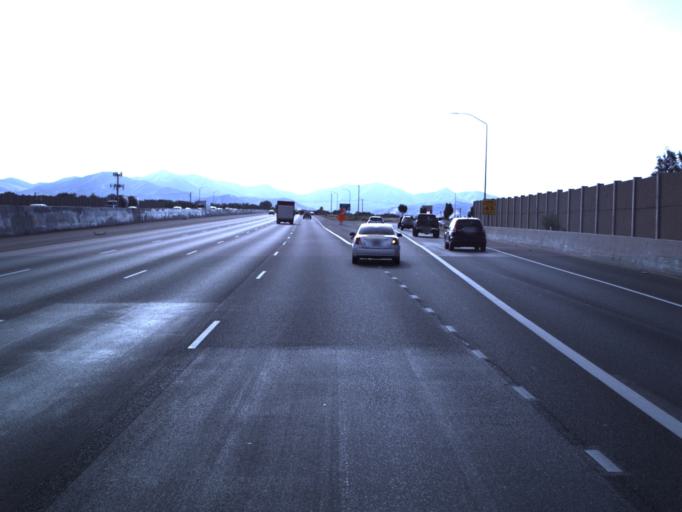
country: US
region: Utah
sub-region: Salt Lake County
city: Taylorsville
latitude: 40.6449
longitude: -111.9325
